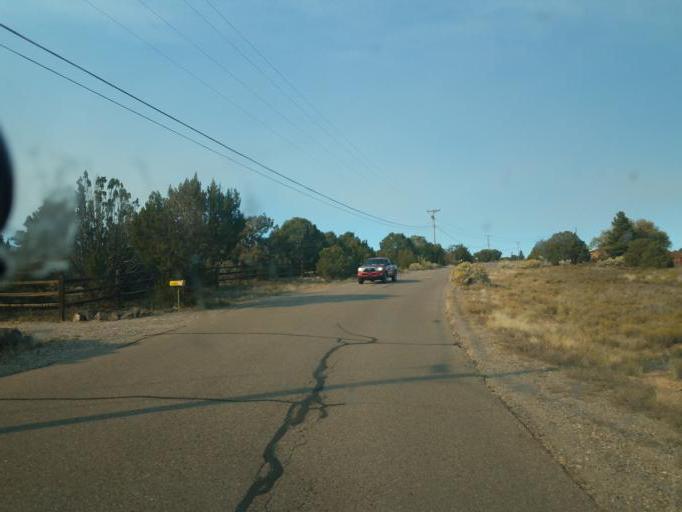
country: US
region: New Mexico
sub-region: Los Alamos County
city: White Rock
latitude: 35.8045
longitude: -106.2183
